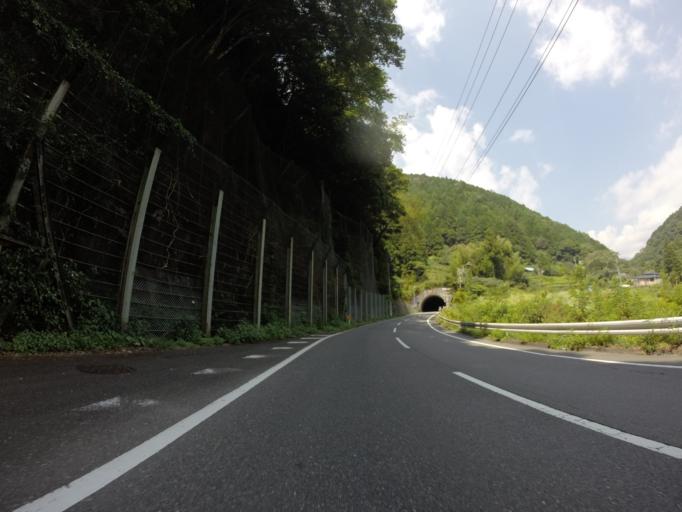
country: JP
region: Shizuoka
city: Shizuoka-shi
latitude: 35.2242
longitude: 138.3495
